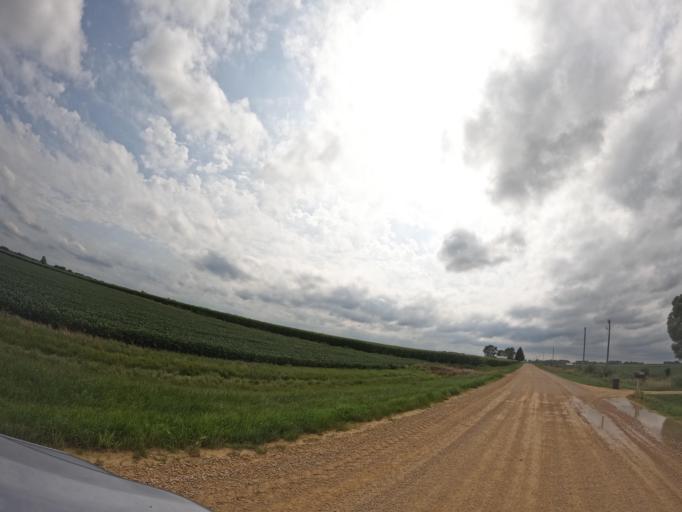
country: US
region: Iowa
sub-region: Clinton County
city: De Witt
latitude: 41.7858
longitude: -90.5724
